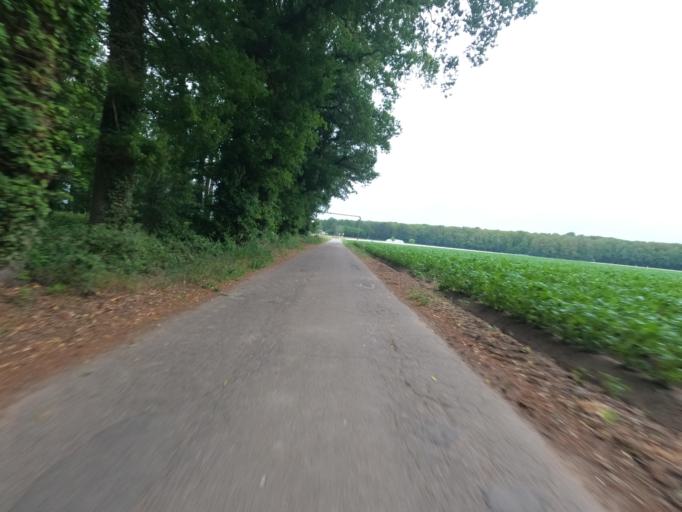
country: DE
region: North Rhine-Westphalia
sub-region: Regierungsbezirk Koln
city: Wassenberg
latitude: 51.1140
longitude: 6.1214
